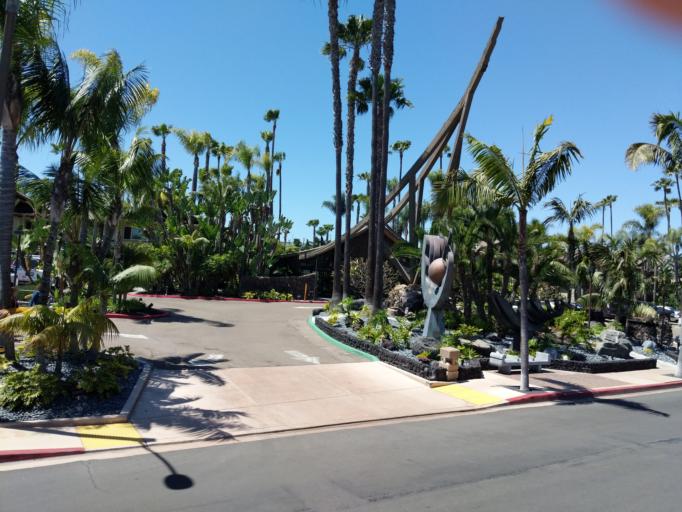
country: US
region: California
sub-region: San Diego County
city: Coronado
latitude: 32.7180
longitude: -117.2232
